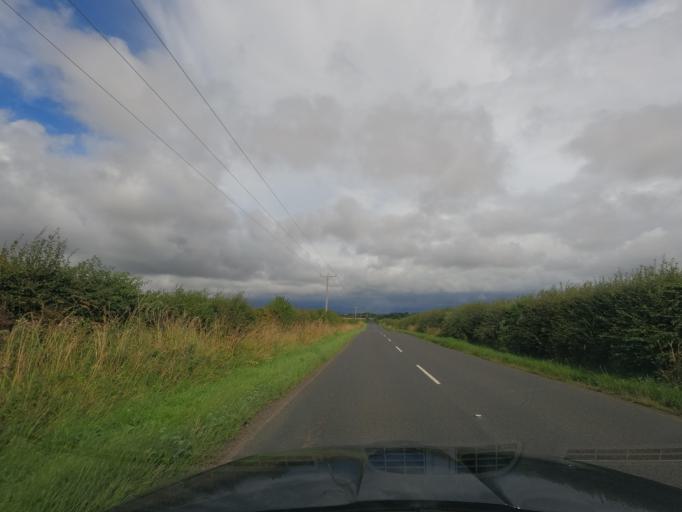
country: GB
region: England
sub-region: Northumberland
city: Ancroft
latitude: 55.6745
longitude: -2.0015
